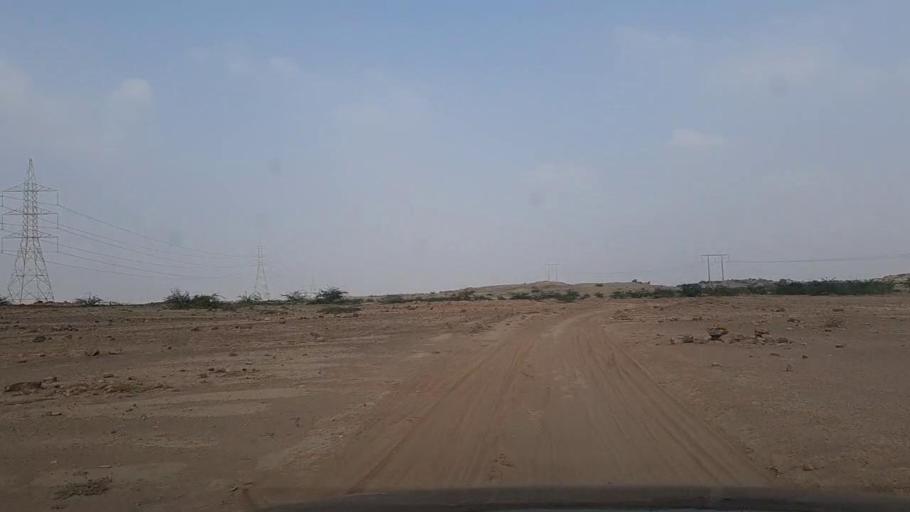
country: PK
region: Sindh
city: Thatta
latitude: 24.8868
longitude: 67.8384
